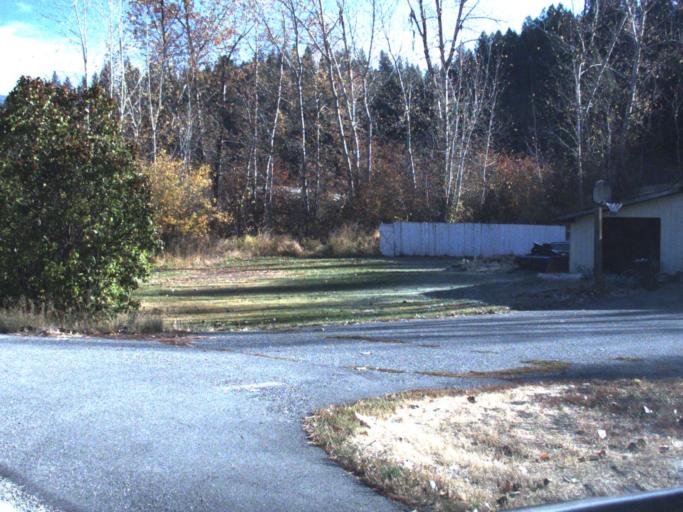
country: US
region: Washington
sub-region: Ferry County
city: Republic
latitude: 48.7826
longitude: -118.6257
